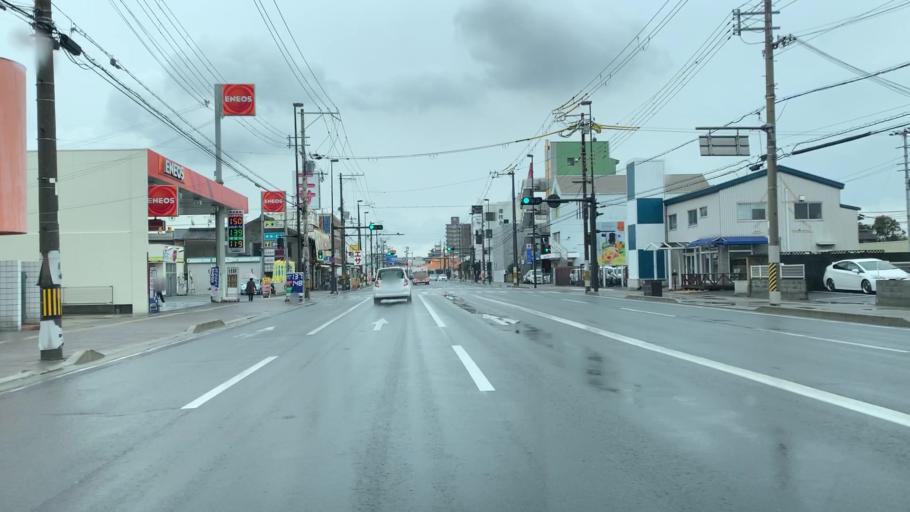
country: JP
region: Wakayama
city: Wakayama-shi
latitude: 34.2270
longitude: 135.1604
